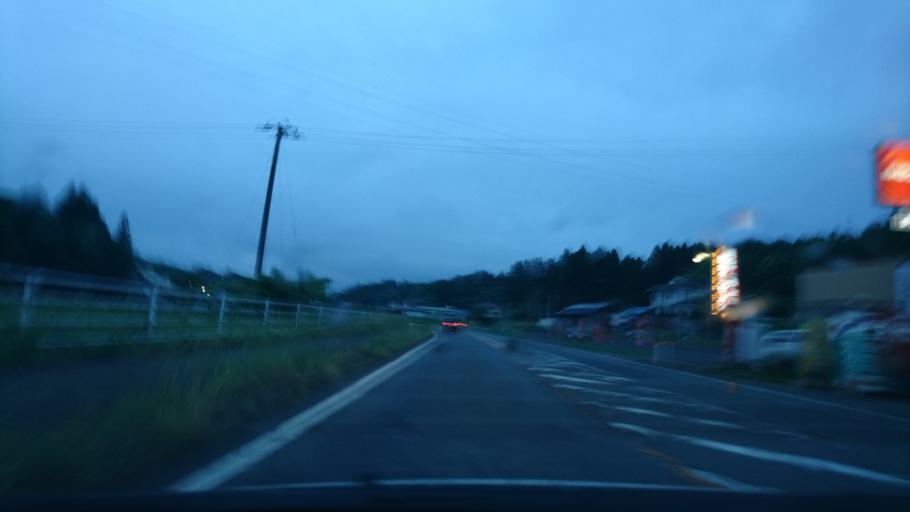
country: JP
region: Iwate
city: Ichinoseki
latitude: 38.7929
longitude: 141.0518
